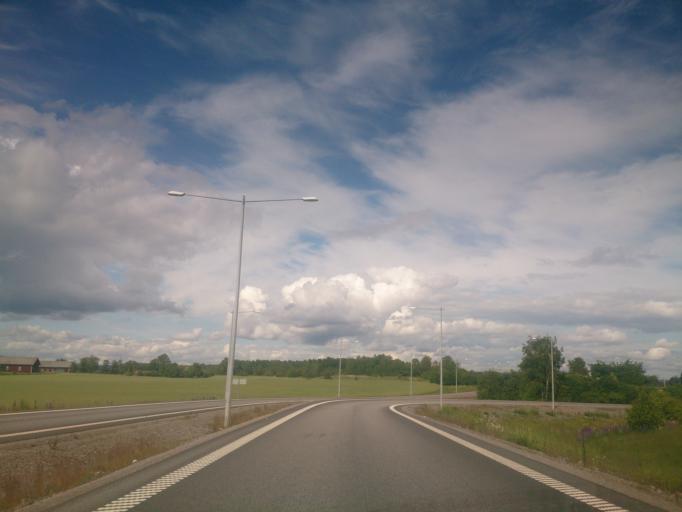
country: SE
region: OEstergoetland
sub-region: Norrkopings Kommun
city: Norrkoping
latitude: 58.6286
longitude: 16.1495
